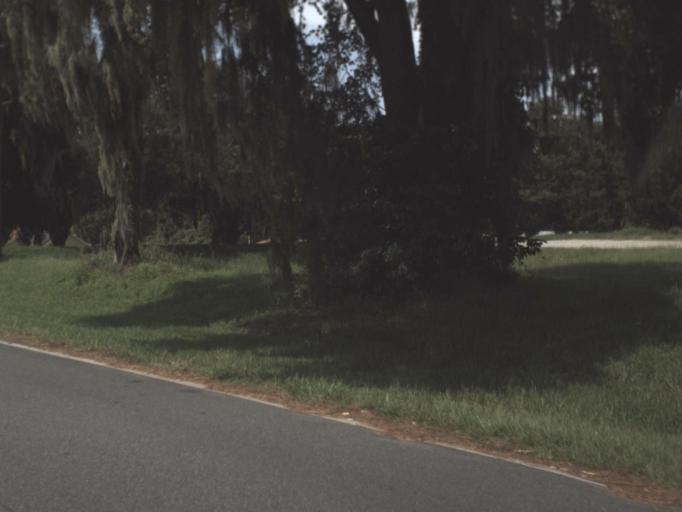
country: US
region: Florida
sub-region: Citrus County
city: Inverness Highlands North
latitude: 28.8735
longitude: -82.3620
